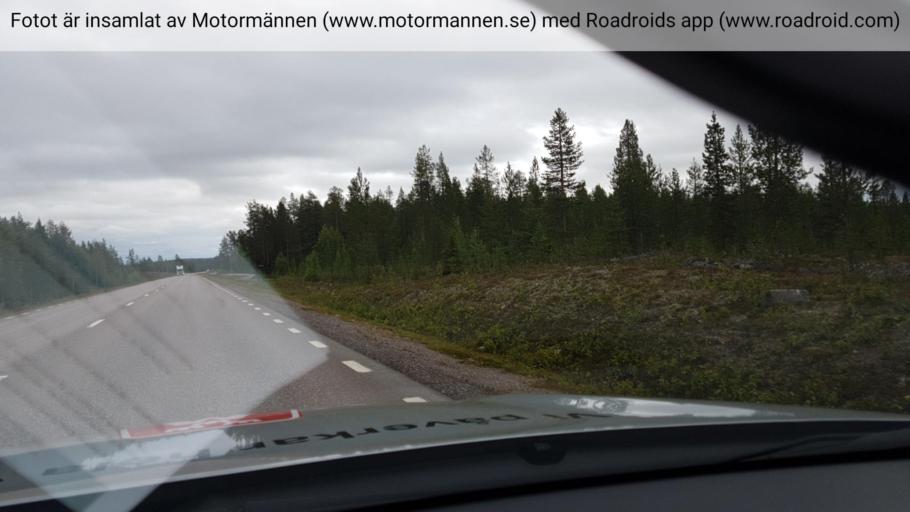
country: SE
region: Norrbotten
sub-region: Gallivare Kommun
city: Gaellivare
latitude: 67.0777
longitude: 21.0769
